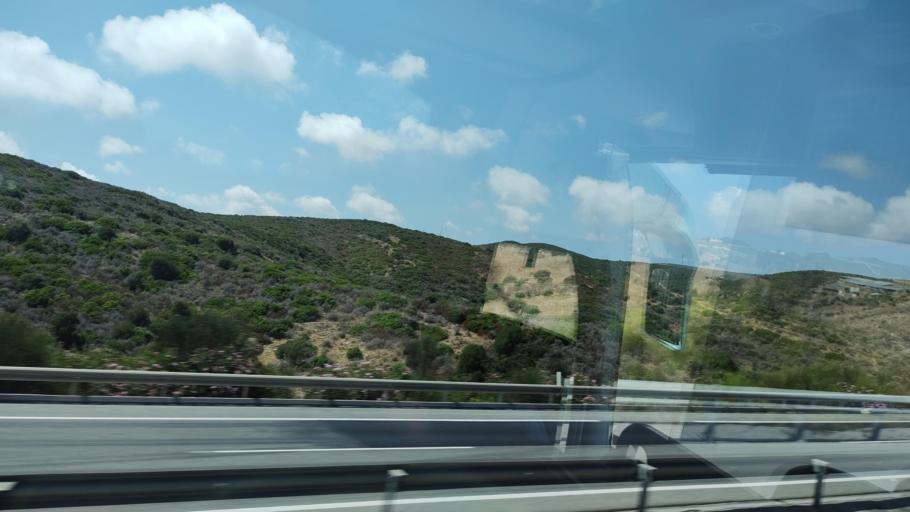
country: ES
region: Andalusia
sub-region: Provincia de Malaga
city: Manilva
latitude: 36.3556
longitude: -5.2694
